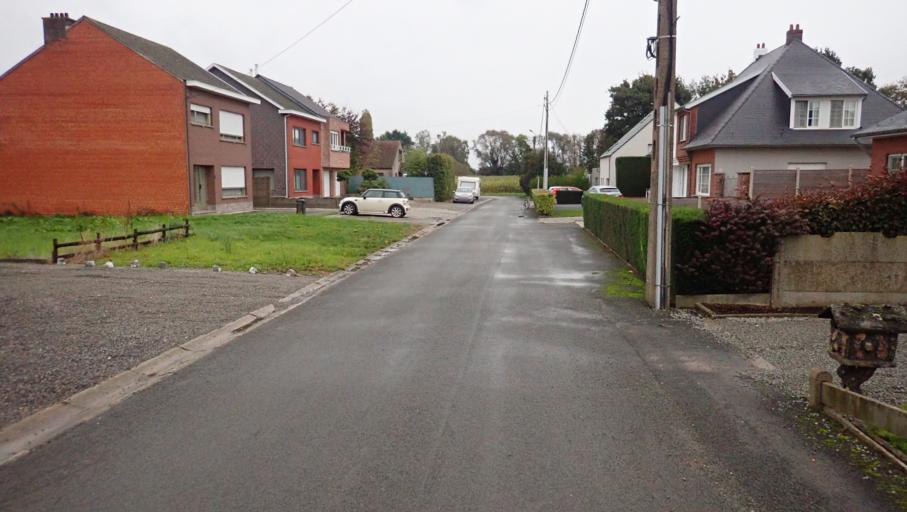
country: BE
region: Flanders
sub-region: Provincie Antwerpen
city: Berlaar
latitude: 51.1094
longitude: 4.6480
